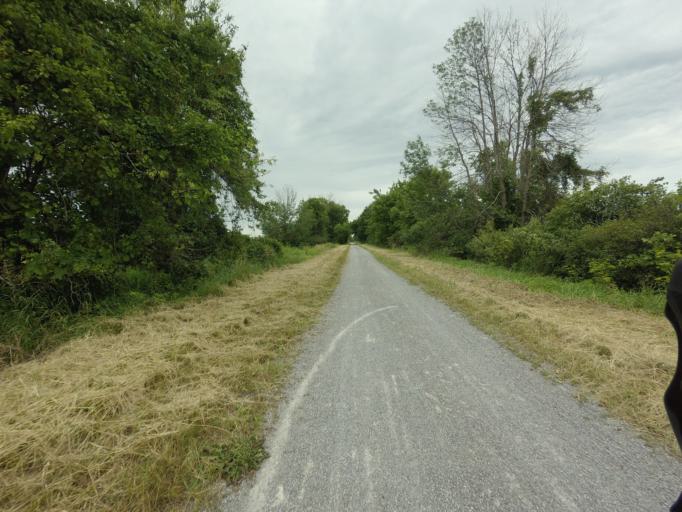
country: CA
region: Ontario
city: Ottawa
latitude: 45.1630
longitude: -75.6155
